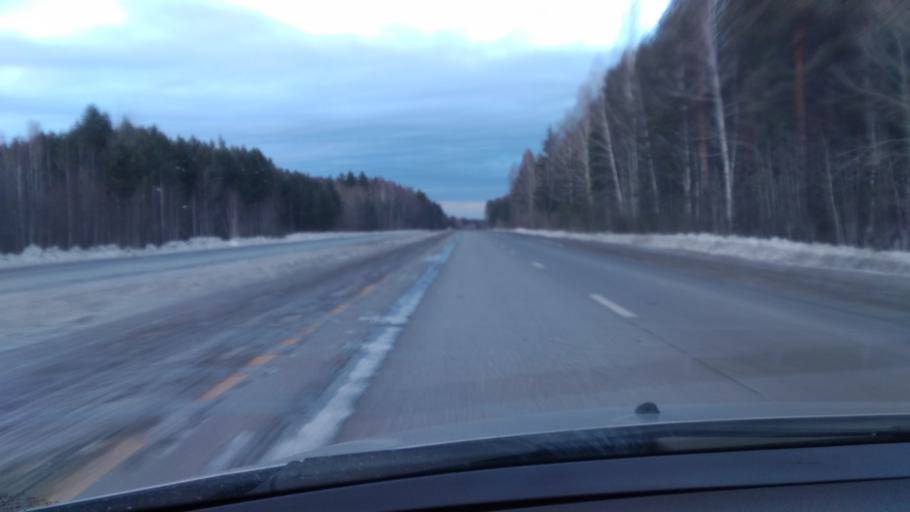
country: RU
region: Sverdlovsk
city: Shchelkun
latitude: 56.3281
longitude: 60.8695
